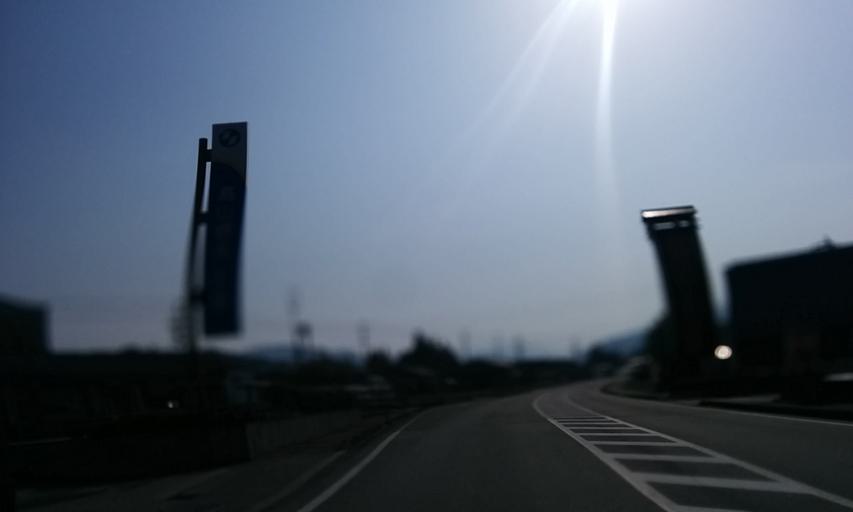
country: JP
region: Gifu
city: Takayama
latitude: 36.1706
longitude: 137.3143
